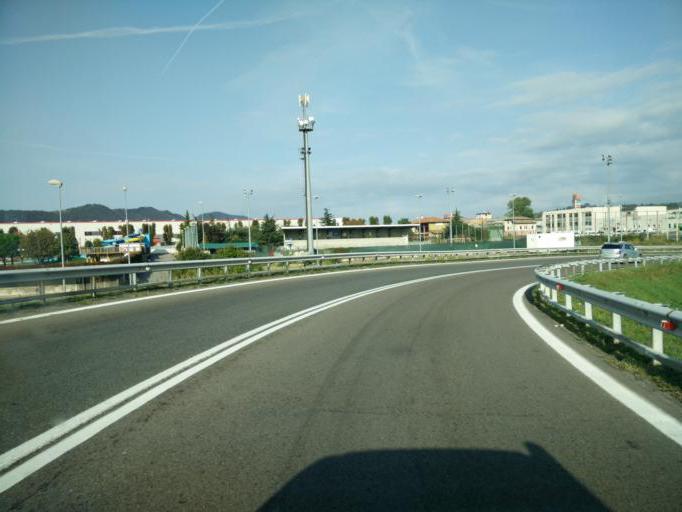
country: IT
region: Lombardy
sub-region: Provincia di Brescia
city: Rovato
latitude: 45.5759
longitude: 10.0067
